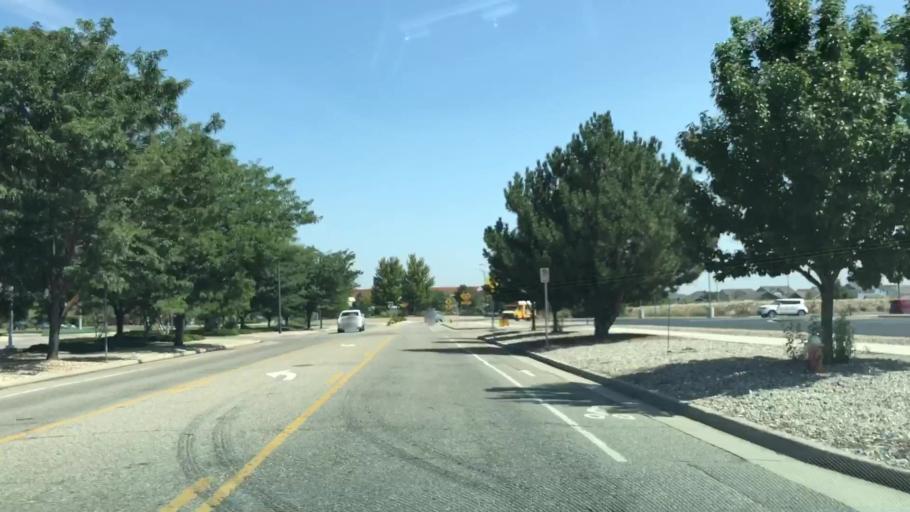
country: US
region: Colorado
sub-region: Larimer County
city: Loveland
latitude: 40.4052
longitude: -105.0414
